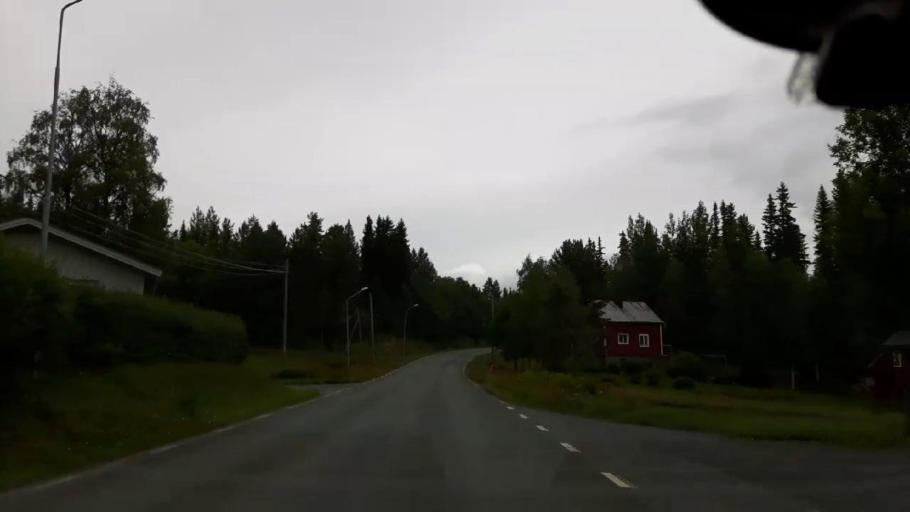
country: SE
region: Jaemtland
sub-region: Krokoms Kommun
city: Valla
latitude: 63.6559
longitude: 13.8285
